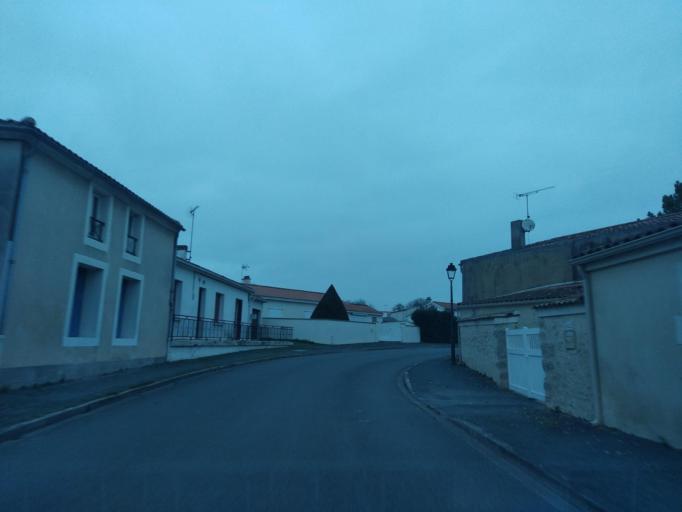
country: FR
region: Pays de la Loire
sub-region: Departement de la Vendee
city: Triaize
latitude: 46.3580
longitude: -1.2497
